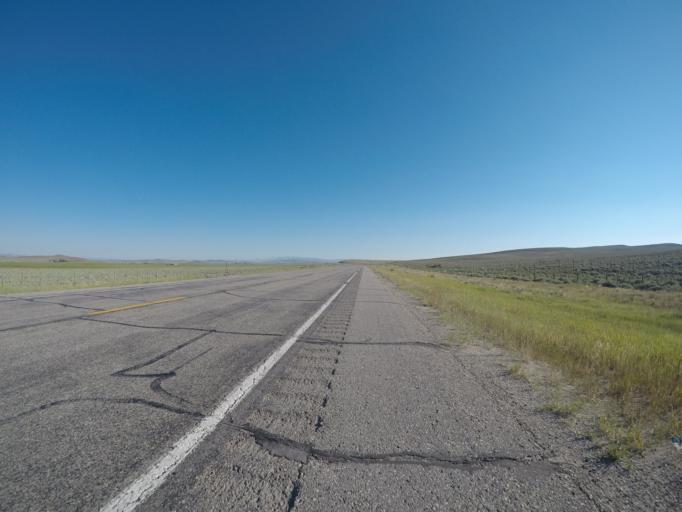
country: US
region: Wyoming
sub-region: Sublette County
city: Pinedale
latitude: 42.9279
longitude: -110.0810
